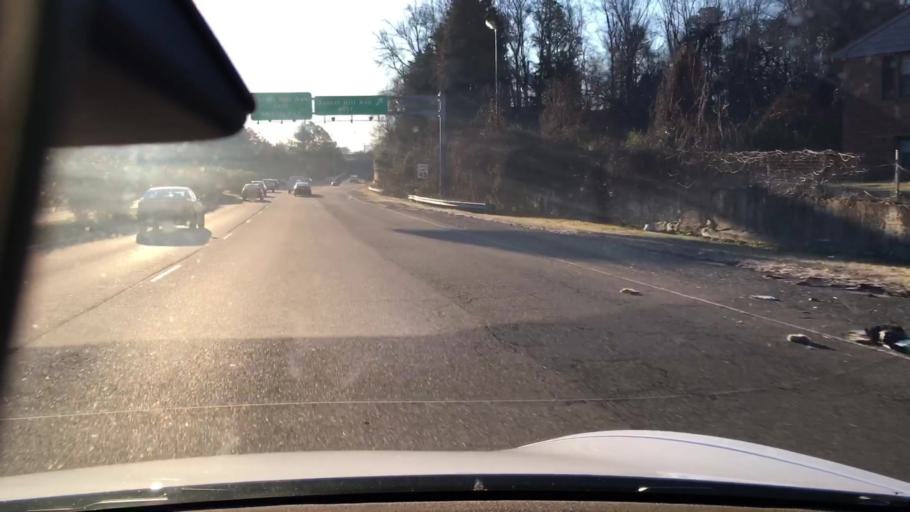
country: US
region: Virginia
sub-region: Chesterfield County
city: Bon Air
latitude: 37.5400
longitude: -77.5321
